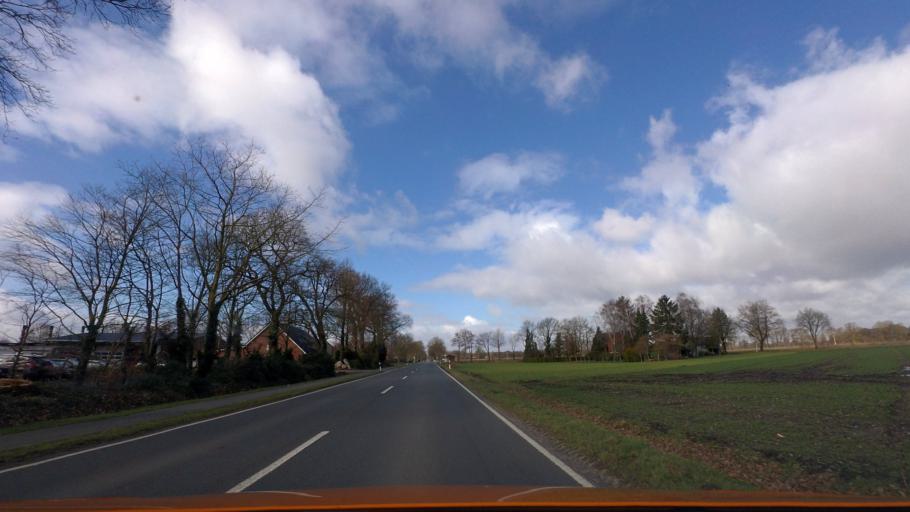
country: DE
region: Lower Saxony
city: Friesoythe
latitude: 53.0161
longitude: 7.9020
